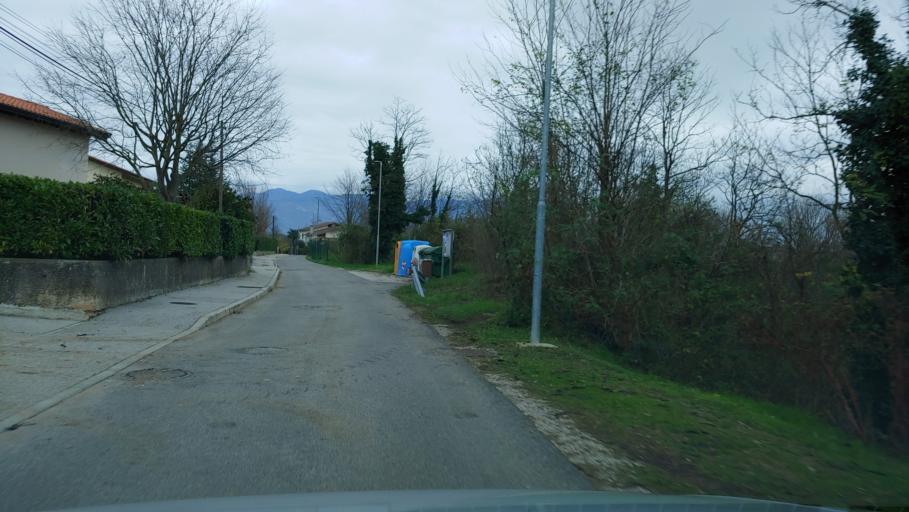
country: SI
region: Miren-Kostanjevica
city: Miren
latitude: 45.8961
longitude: 13.6132
